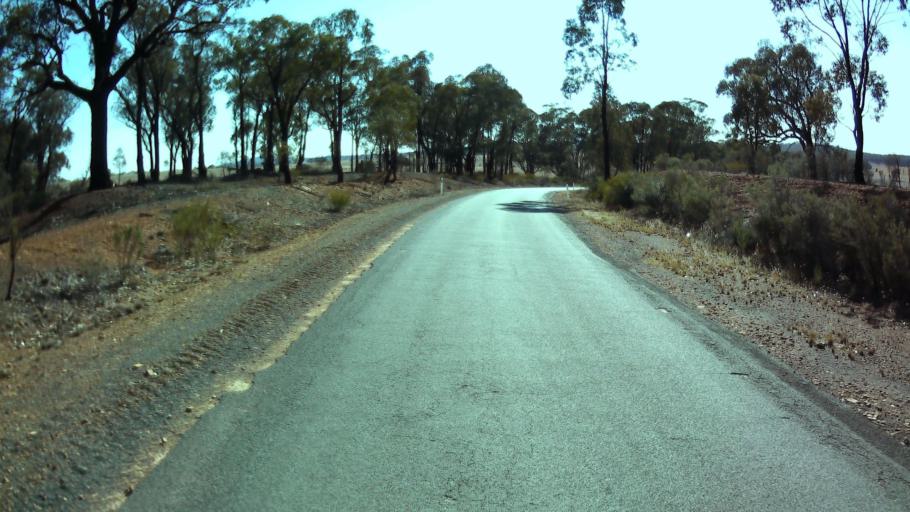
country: AU
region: New South Wales
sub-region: Weddin
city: Grenfell
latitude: -33.7824
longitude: 147.9614
